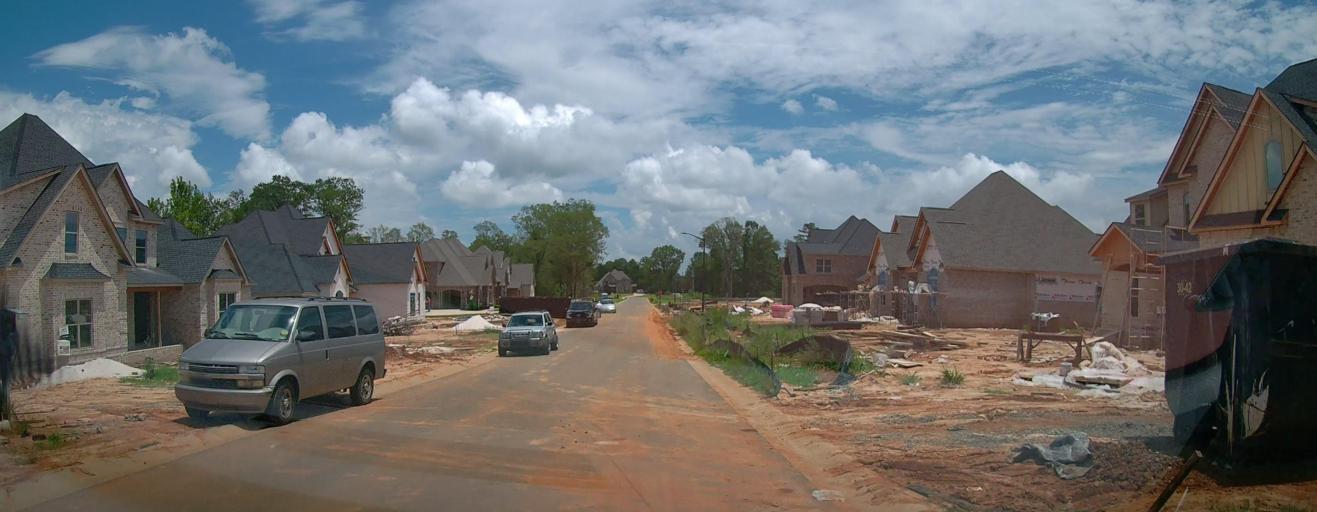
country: US
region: Georgia
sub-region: Houston County
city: Robins Air Force Base
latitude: 32.5144
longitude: -83.6257
